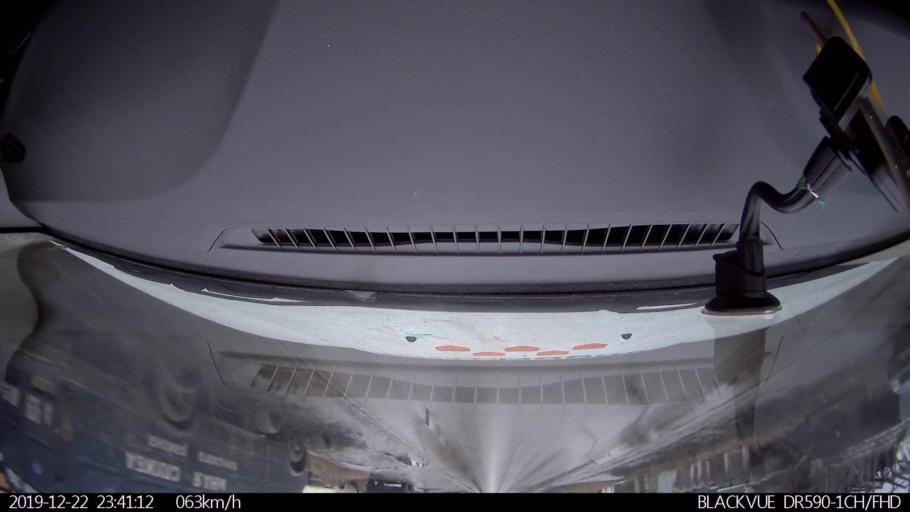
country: RU
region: Nizjnij Novgorod
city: Nizhniy Novgorod
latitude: 56.2833
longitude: 43.9106
